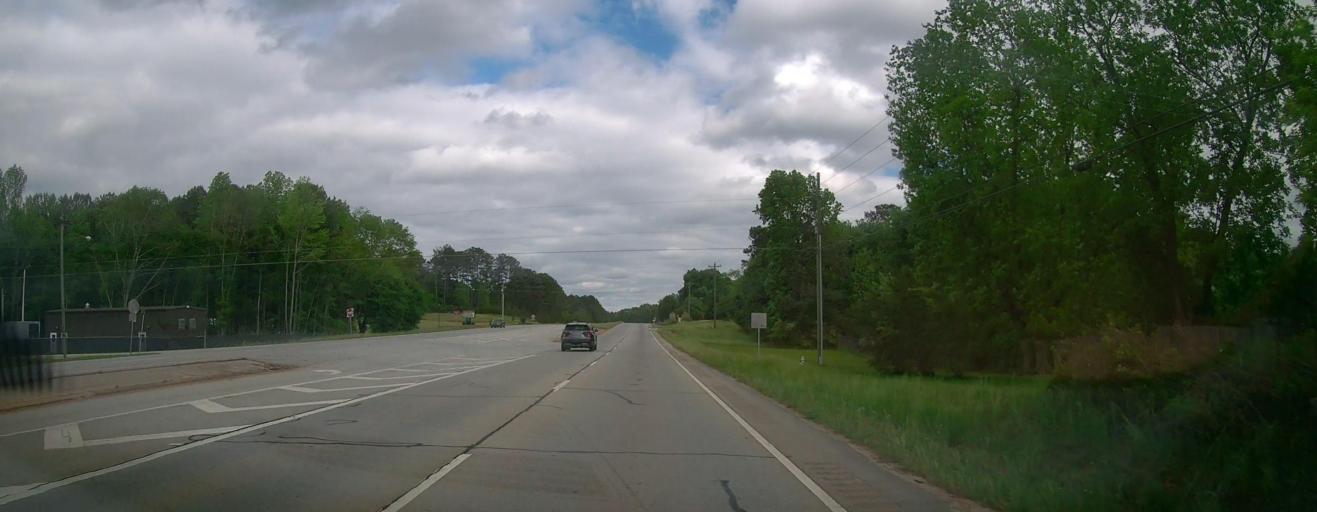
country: US
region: Georgia
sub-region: Walton County
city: Monroe
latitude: 33.8084
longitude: -83.7935
